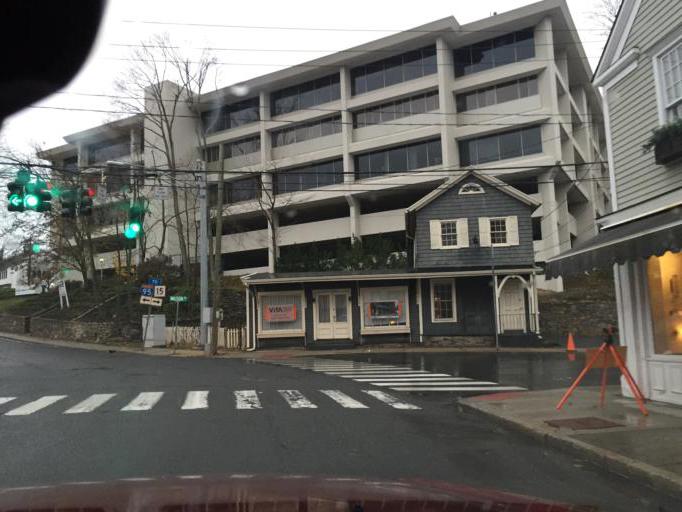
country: US
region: Connecticut
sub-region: Fairfield County
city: Westport
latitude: 41.1407
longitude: -73.3644
